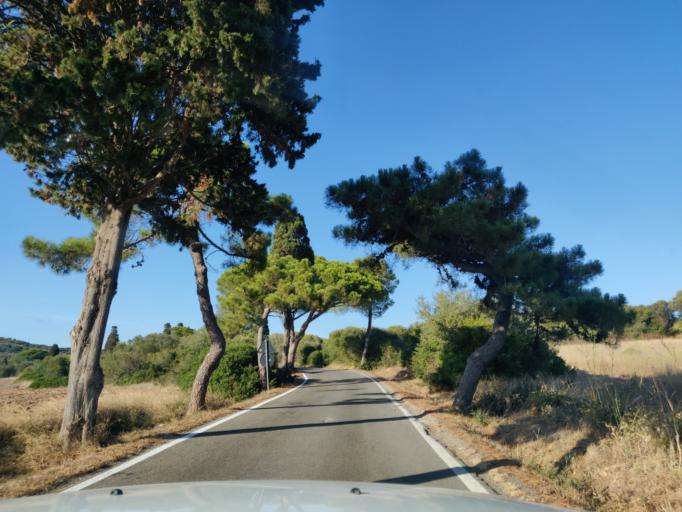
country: IT
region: Tuscany
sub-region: Provincia di Grosseto
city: Orbetello Scalo
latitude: 42.4146
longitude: 11.2986
